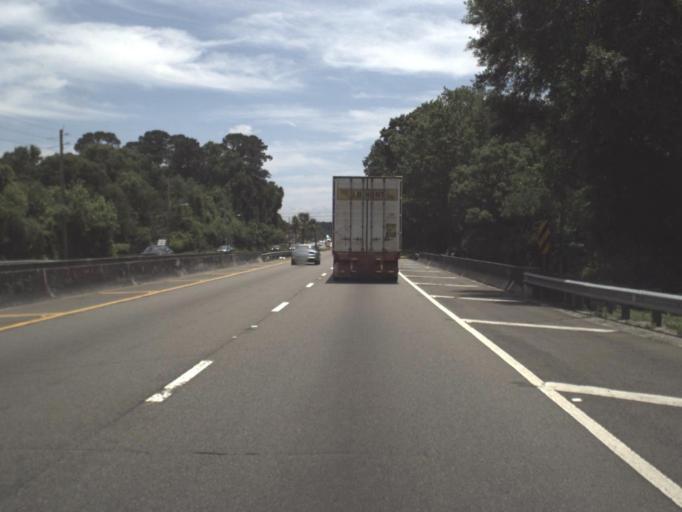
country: US
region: Florida
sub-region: Duval County
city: Jacksonville
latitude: 30.3754
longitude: -81.7270
